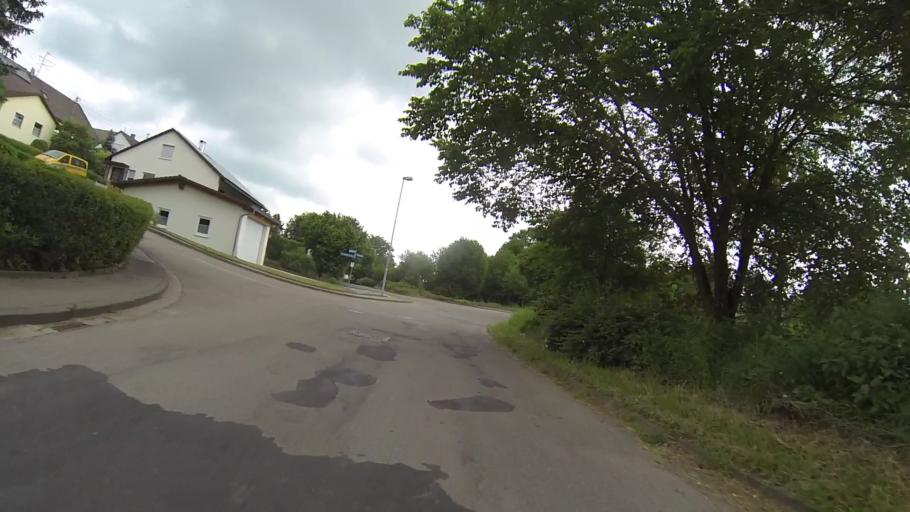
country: DE
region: Baden-Wuerttemberg
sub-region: Regierungsbezirk Stuttgart
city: Bohmenkirch
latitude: 48.6699
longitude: 9.9876
